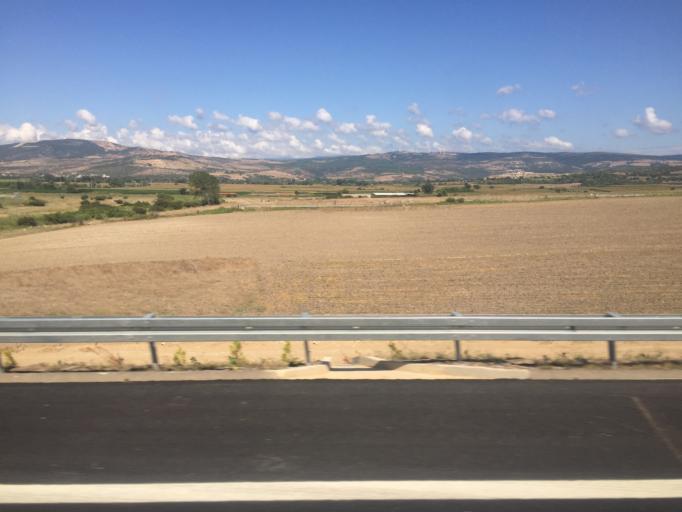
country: TR
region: Bursa
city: Karacabey
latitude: 40.2336
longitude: 28.4183
